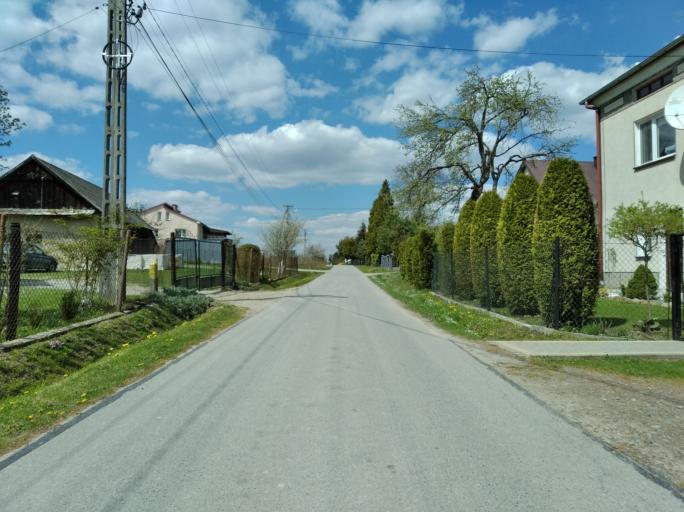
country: PL
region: Subcarpathian Voivodeship
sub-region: Powiat brzozowski
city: Jablonka
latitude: 49.7371
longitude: 22.0936
